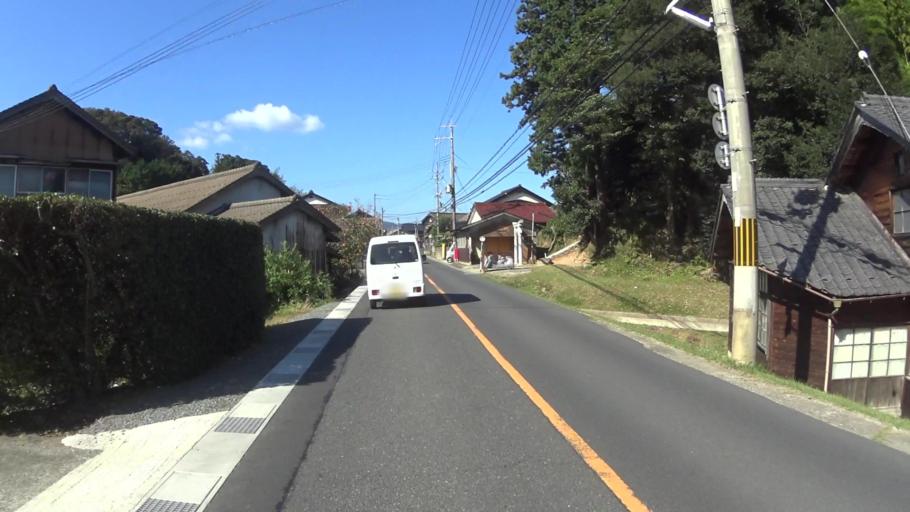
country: JP
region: Kyoto
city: Miyazu
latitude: 35.6824
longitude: 135.0487
